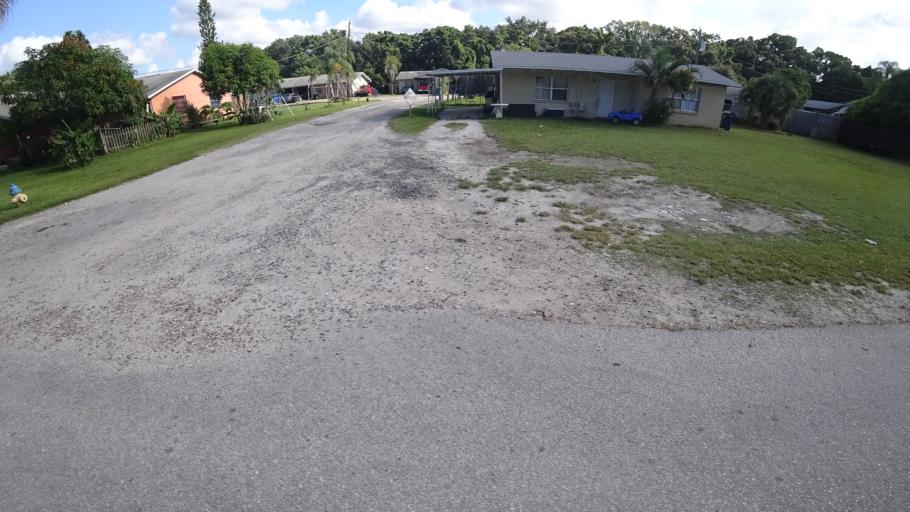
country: US
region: Florida
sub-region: Manatee County
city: Whitfield
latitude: 27.4367
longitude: -82.5579
